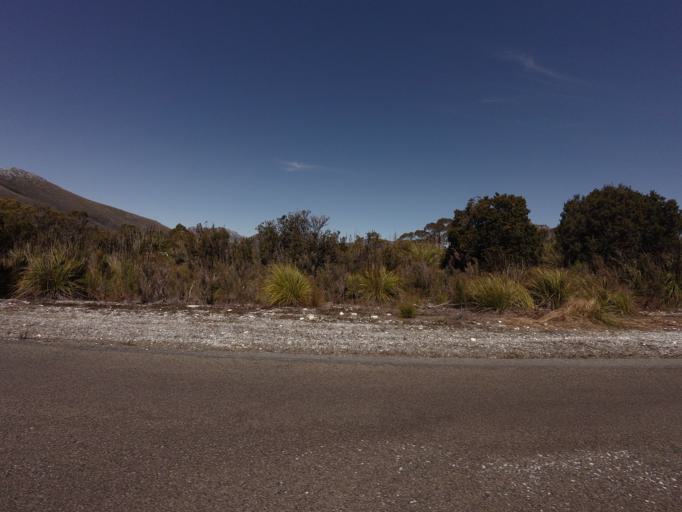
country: AU
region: Tasmania
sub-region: Huon Valley
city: Geeveston
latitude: -42.8356
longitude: 146.1450
